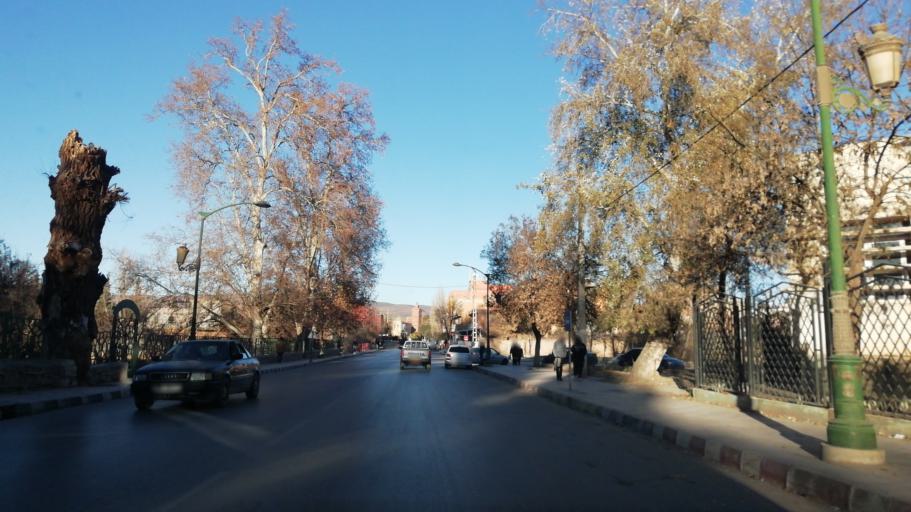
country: DZ
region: Tlemcen
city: Sebdou
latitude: 34.6421
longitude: -1.3279
